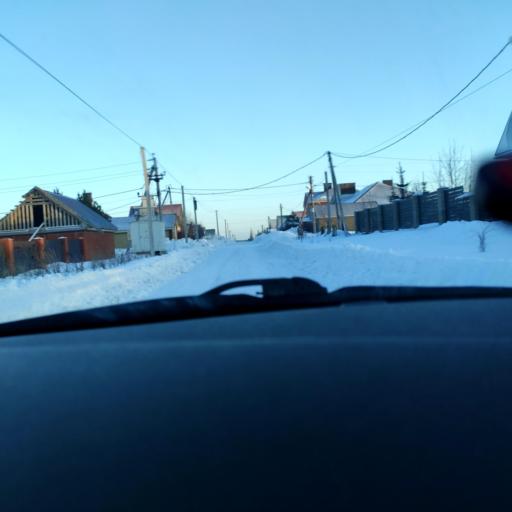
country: RU
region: Bashkortostan
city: Kabakovo
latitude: 54.6338
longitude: 56.1027
